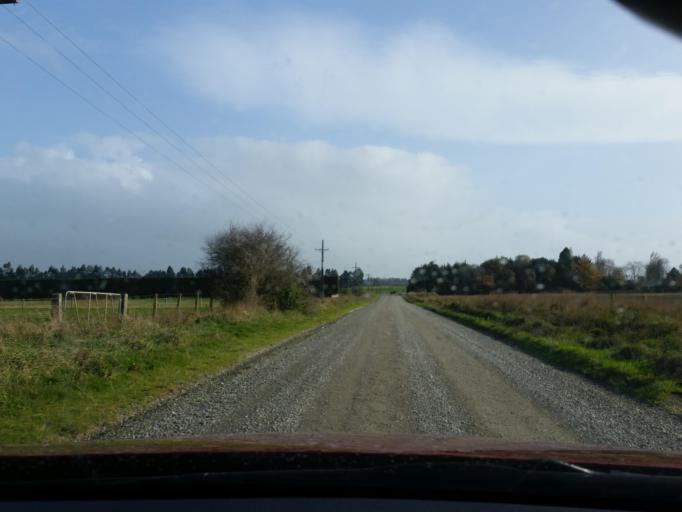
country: NZ
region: Southland
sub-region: Invercargill City
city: Invercargill
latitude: -46.2916
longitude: 168.4176
